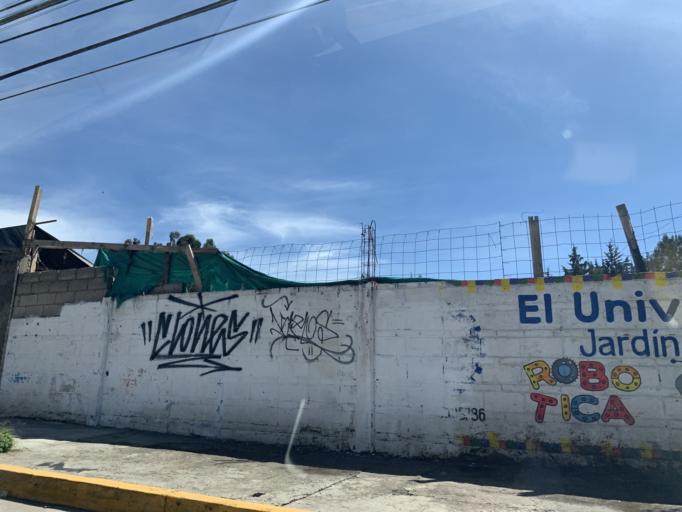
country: MX
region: Puebla
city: Cuautlancingo
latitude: 19.1018
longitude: -98.2738
